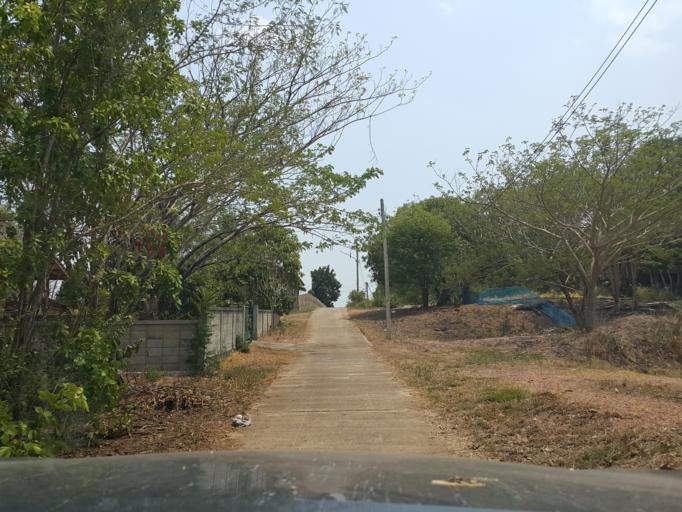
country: TH
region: Lampang
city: Mae Phrik
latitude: 17.5679
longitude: 99.0861
